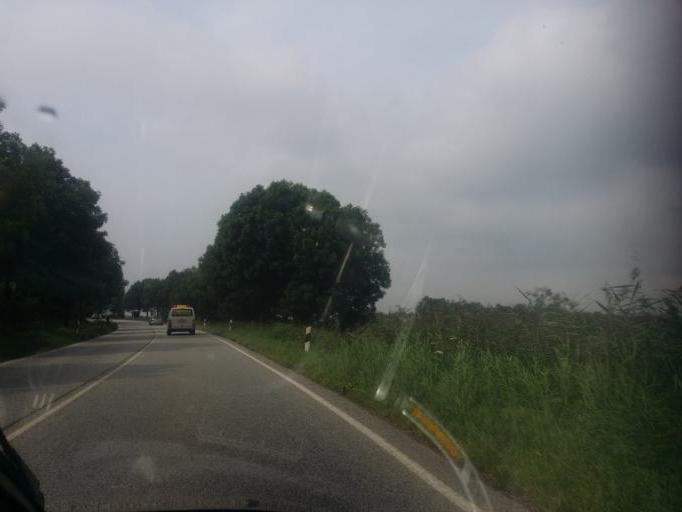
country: DE
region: Schleswig-Holstein
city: Koldenbuttel
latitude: 54.4300
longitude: 9.0544
